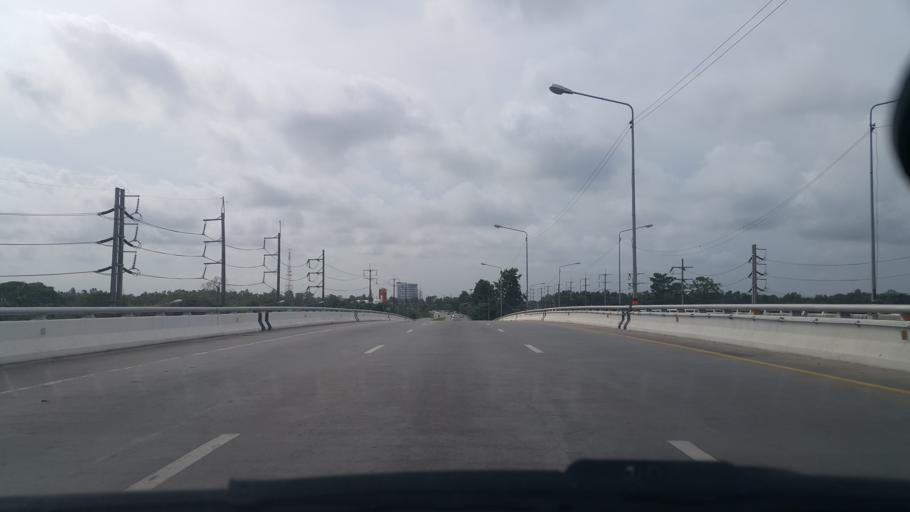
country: TH
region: Rayong
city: Rayong
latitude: 12.6837
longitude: 101.2994
